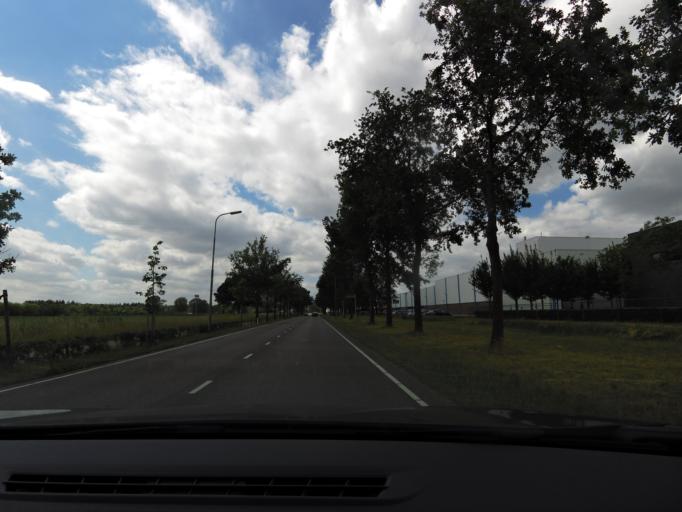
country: NL
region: North Brabant
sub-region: Gemeente Dongen
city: Dongen
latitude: 51.6154
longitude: 4.9233
